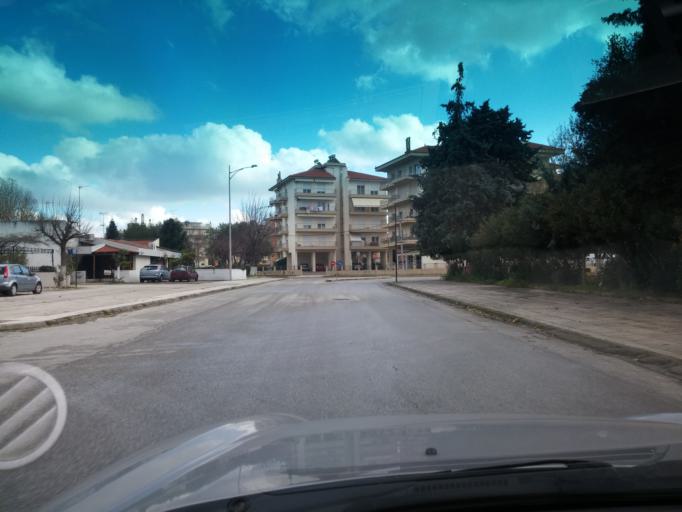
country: GR
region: East Macedonia and Thrace
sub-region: Nomos Rodopis
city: Komotini
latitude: 41.1213
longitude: 25.3911
